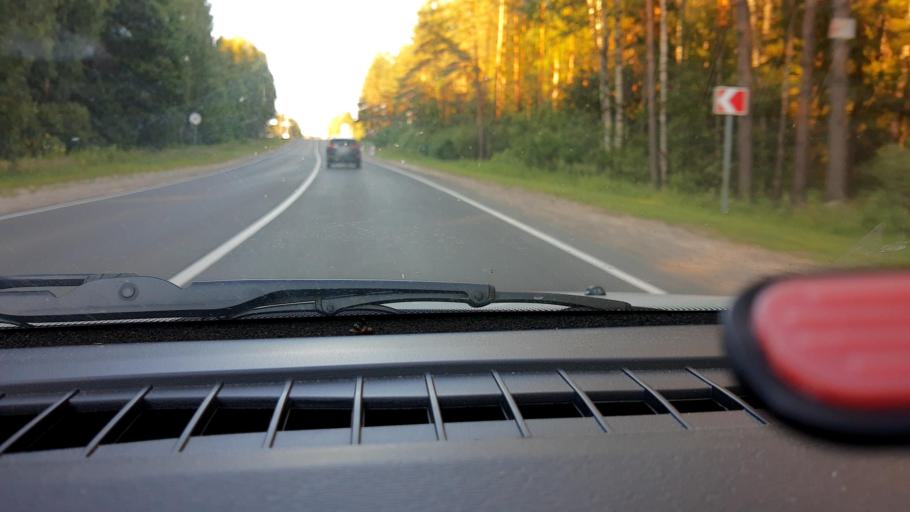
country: RU
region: Nizjnij Novgorod
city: Semenov
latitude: 56.8193
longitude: 44.5708
